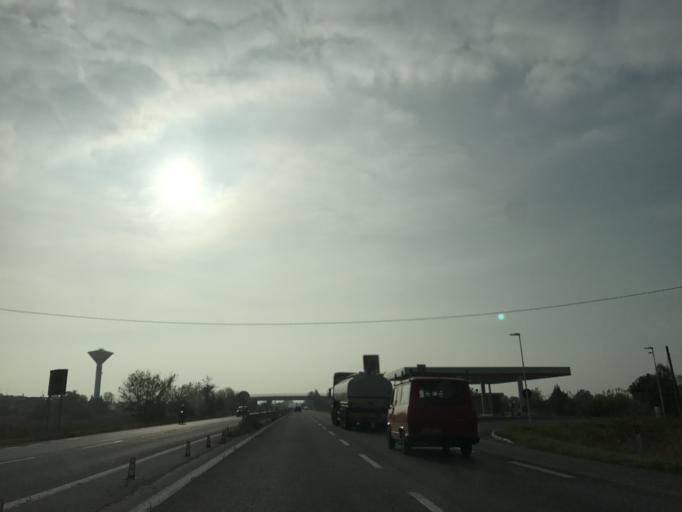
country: IT
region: Emilia-Romagna
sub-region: Forli-Cesena
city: Gatteo a Mare
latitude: 44.1759
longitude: 12.4158
